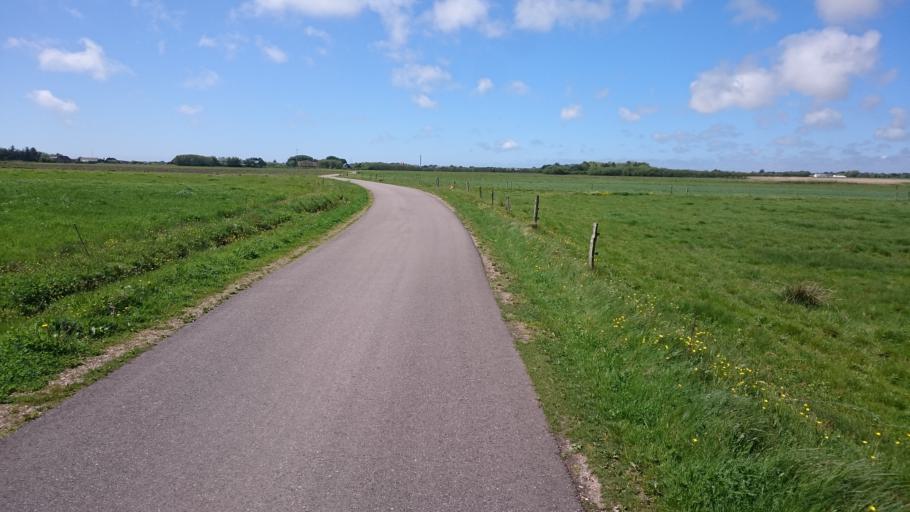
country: DK
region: South Denmark
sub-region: Fano Kommune
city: Nordby
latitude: 55.4252
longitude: 8.4099
